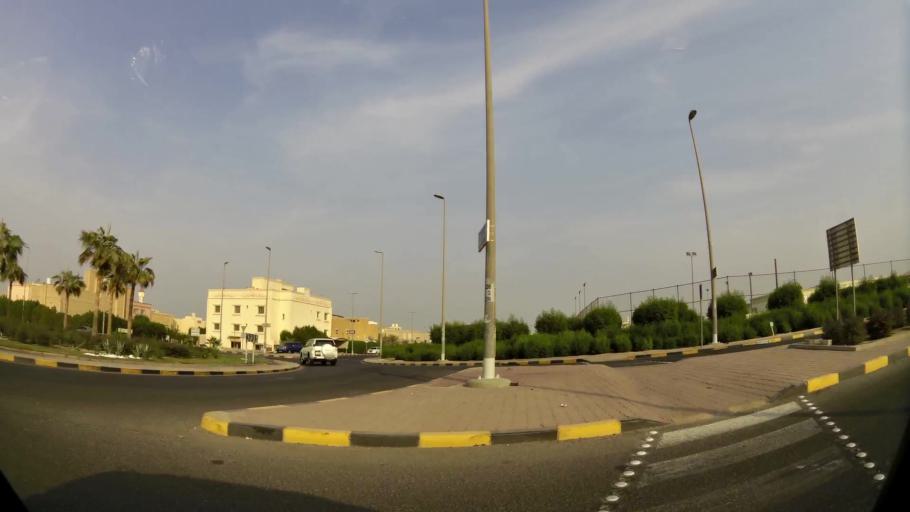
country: KW
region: Mubarak al Kabir
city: Mubarak al Kabir
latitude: 29.2034
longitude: 48.0690
